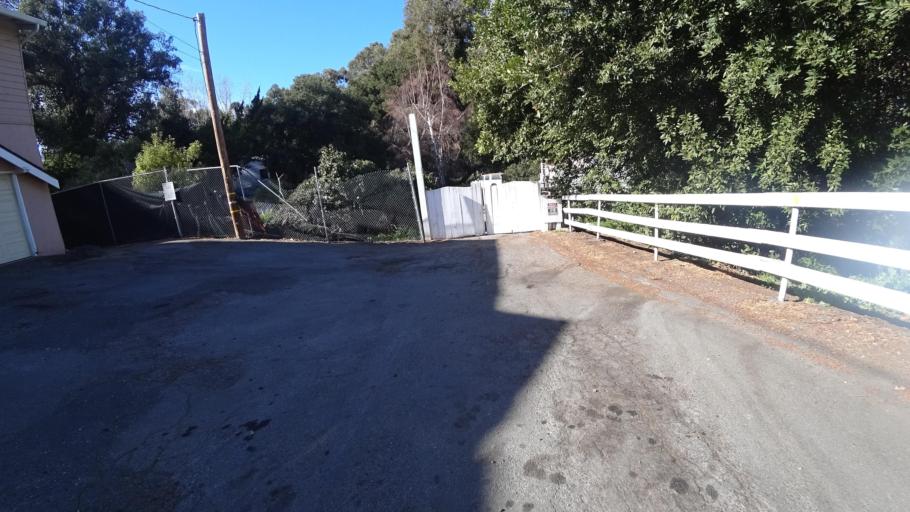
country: US
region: California
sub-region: Alameda County
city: Hayward
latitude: 37.6797
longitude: -122.0788
